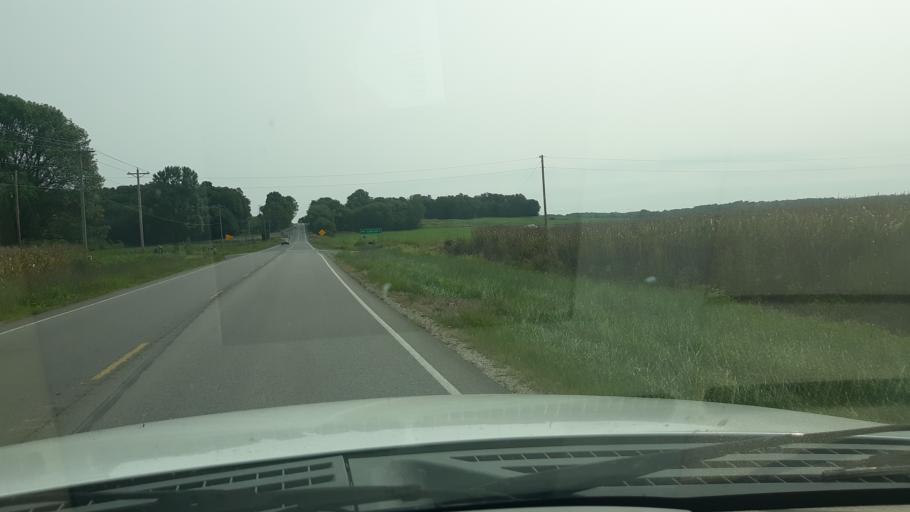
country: US
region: Indiana
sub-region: Gibson County
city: Owensville
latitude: 38.3558
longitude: -87.6652
